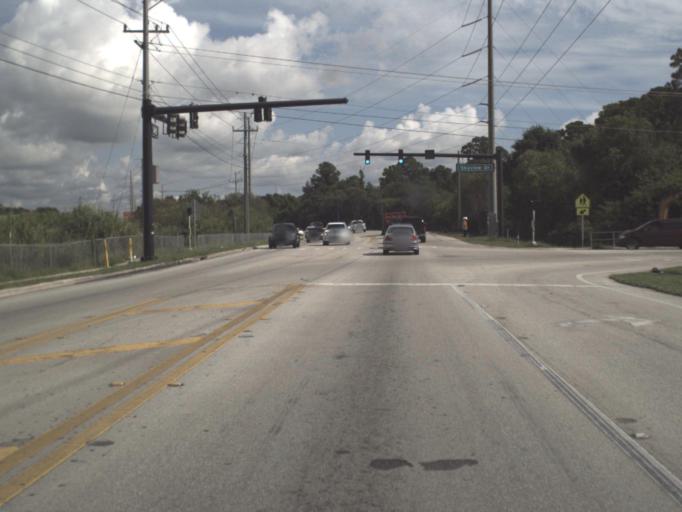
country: US
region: Florida
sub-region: Polk County
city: Crystal Lake
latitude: 28.0256
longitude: -81.9077
